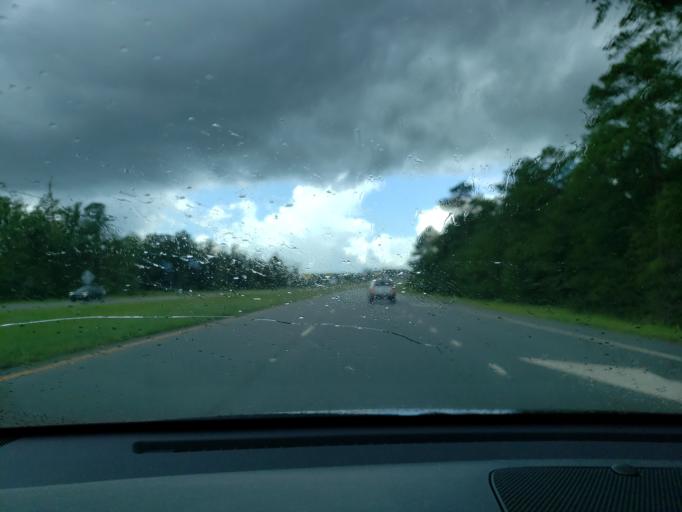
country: US
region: North Carolina
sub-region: Bladen County
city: Elizabethtown
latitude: 34.6037
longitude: -78.6181
